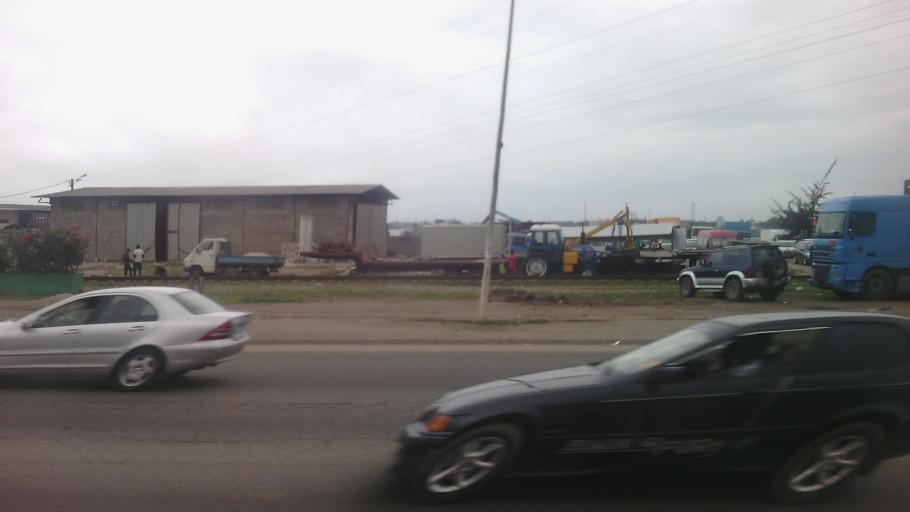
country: CI
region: Lagunes
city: Abidjan
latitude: 5.2713
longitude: -3.9632
